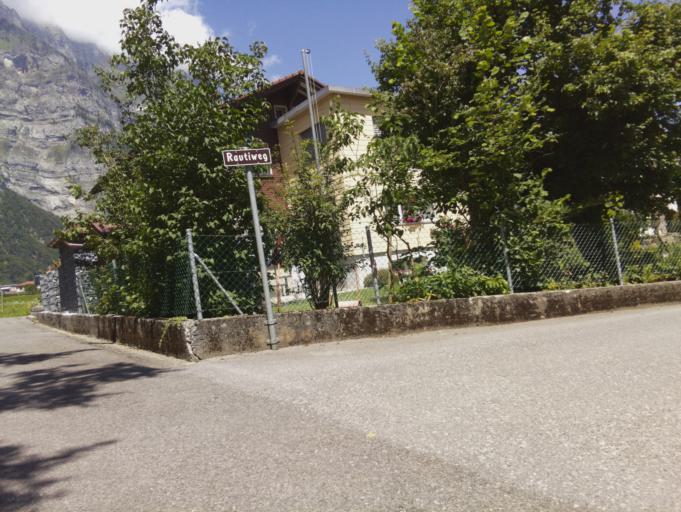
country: CH
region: Glarus
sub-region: Glarus
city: Glarus
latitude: 47.0473
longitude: 9.0577
